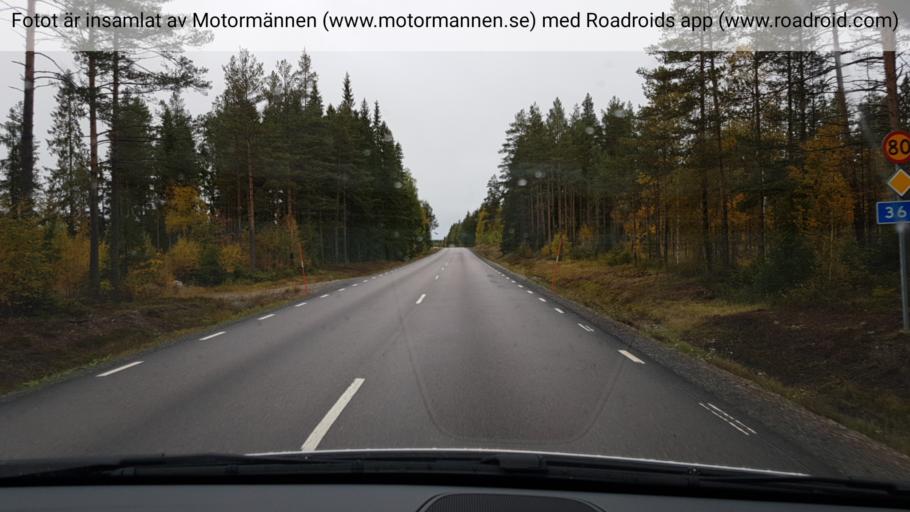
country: SE
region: Vaesterbotten
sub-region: Umea Kommun
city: Ersmark
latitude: 63.9465
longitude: 20.3021
